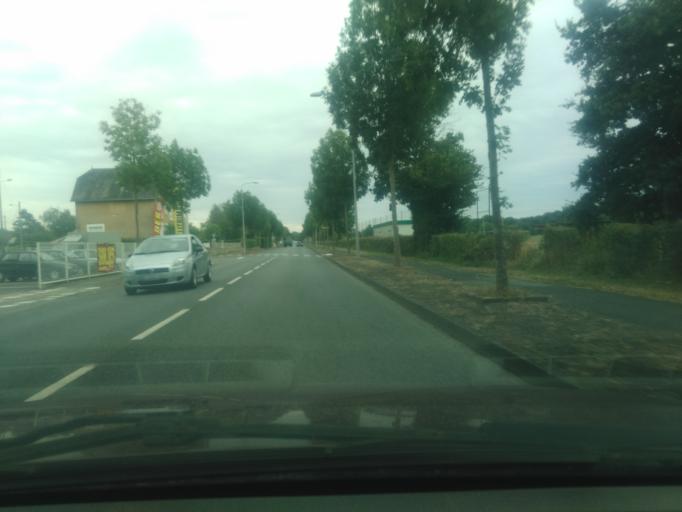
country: FR
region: Centre
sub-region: Departement de l'Indre
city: Le Blanc
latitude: 46.6318
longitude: 1.0842
